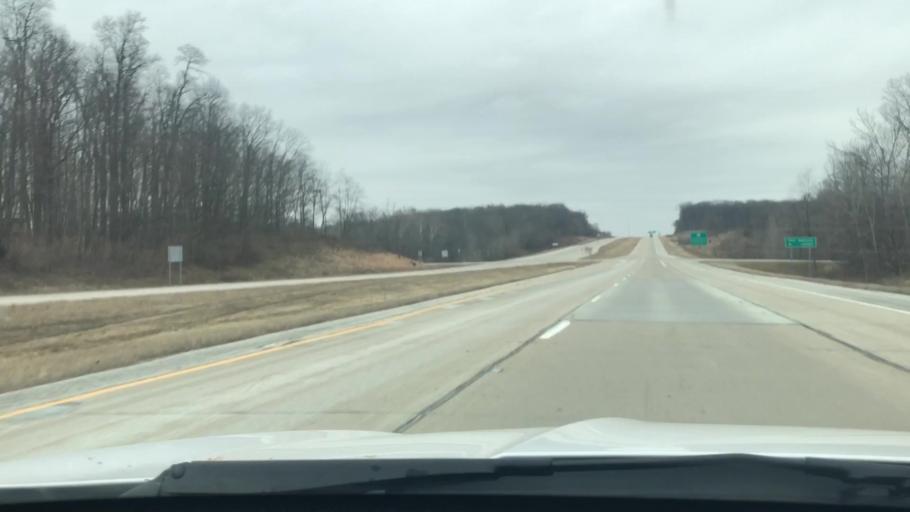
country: US
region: Indiana
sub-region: Miami County
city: Peru
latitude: 40.7701
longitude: -86.1512
